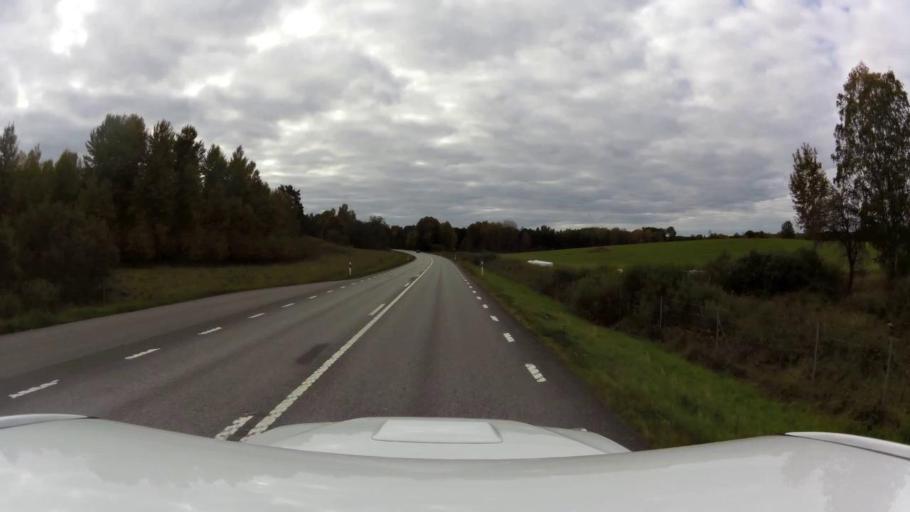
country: SE
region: OEstergoetland
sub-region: Kinda Kommun
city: Rimforsa
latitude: 58.1908
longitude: 15.6666
